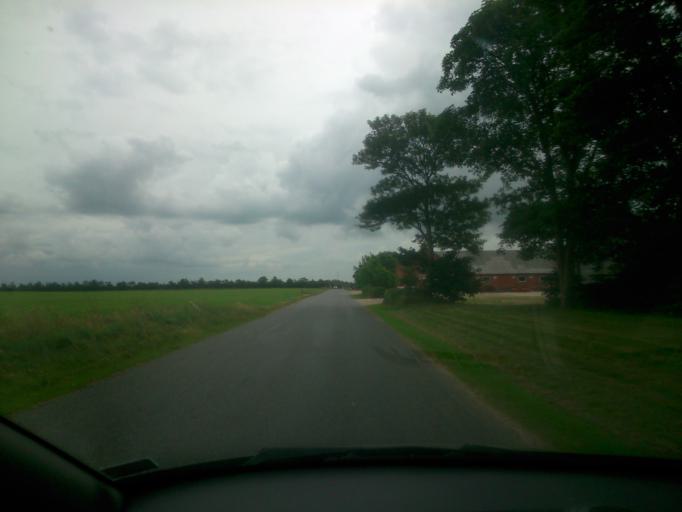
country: DK
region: South Denmark
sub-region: Varde Kommune
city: Varde
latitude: 55.5574
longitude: 8.4378
